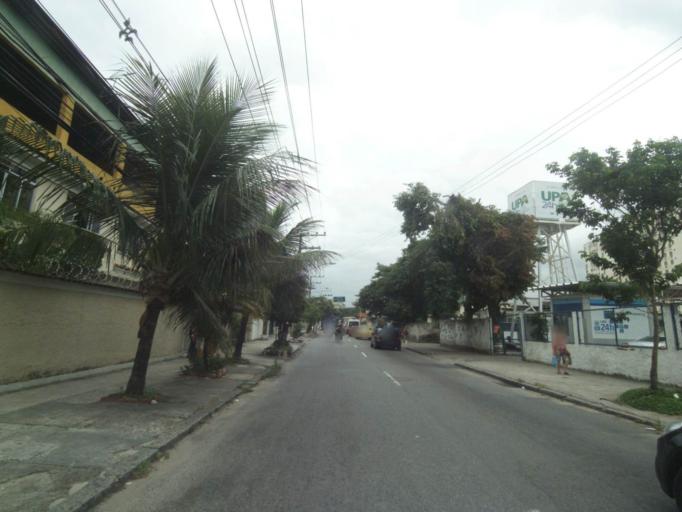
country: BR
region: Rio de Janeiro
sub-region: Sao Joao De Meriti
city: Sao Joao de Meriti
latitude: -22.9232
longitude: -43.3693
